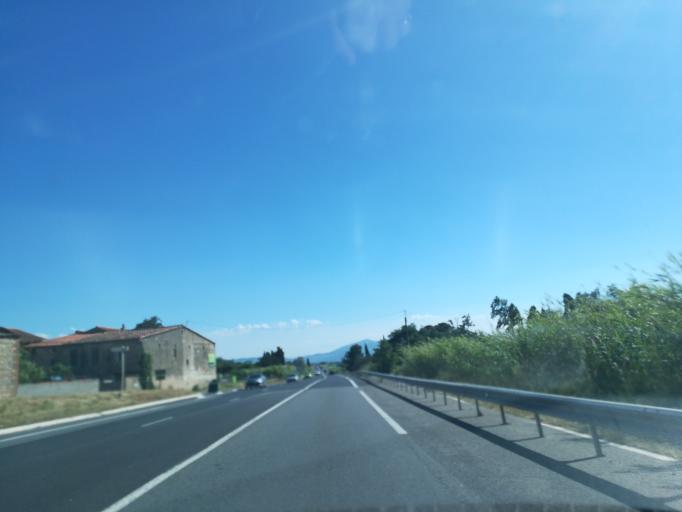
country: FR
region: Languedoc-Roussillon
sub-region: Departement des Pyrenees-Orientales
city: Villemolaque
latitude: 42.5968
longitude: 2.8553
